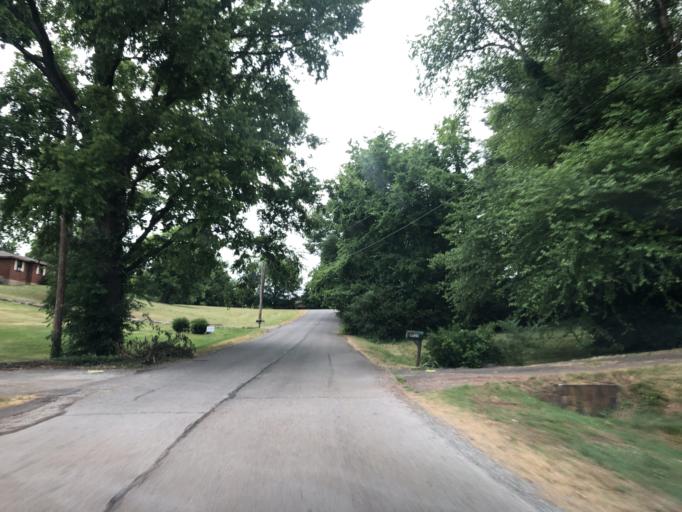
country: US
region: Tennessee
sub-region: Davidson County
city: Goodlettsville
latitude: 36.2647
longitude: -86.7713
